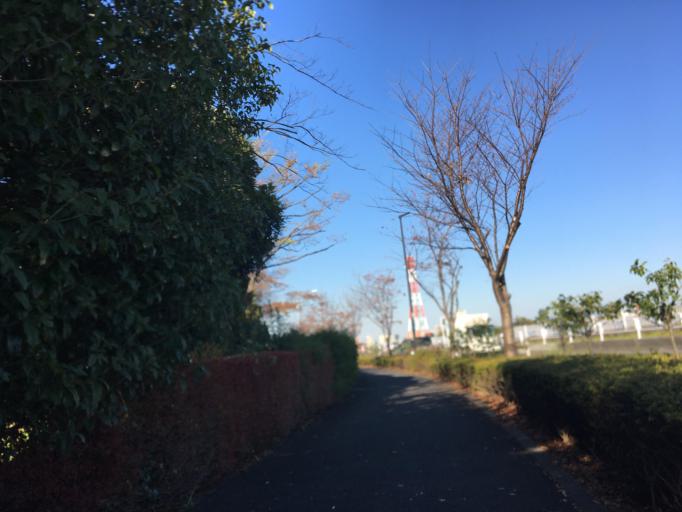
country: JP
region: Tokyo
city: Urayasu
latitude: 35.6983
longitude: 139.9177
